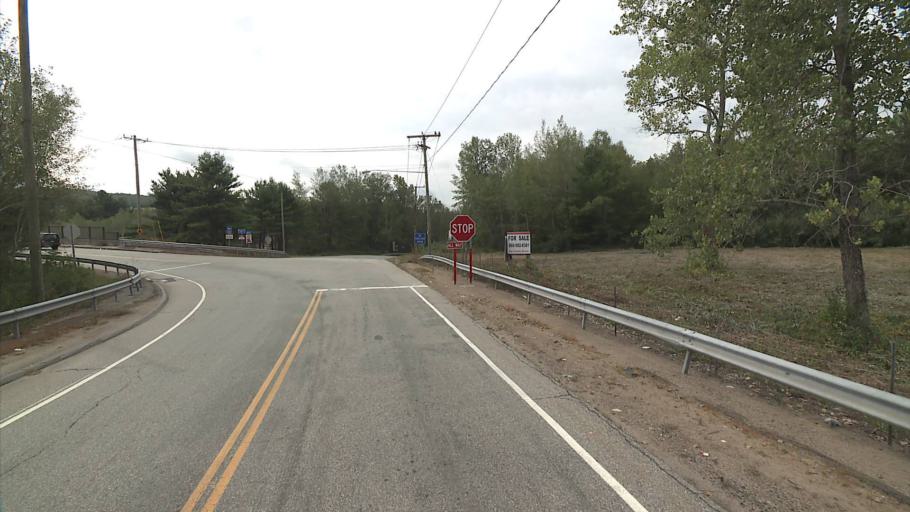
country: US
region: Connecticut
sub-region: Tolland County
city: Stafford Springs
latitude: 41.9235
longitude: -72.2610
